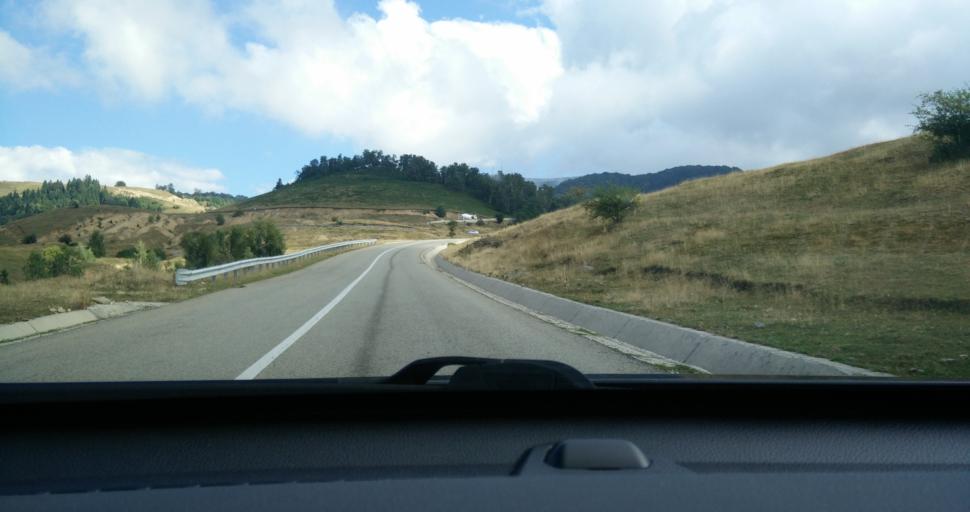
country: RO
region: Gorj
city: Novaci-Straini
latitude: 45.2162
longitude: 23.6984
